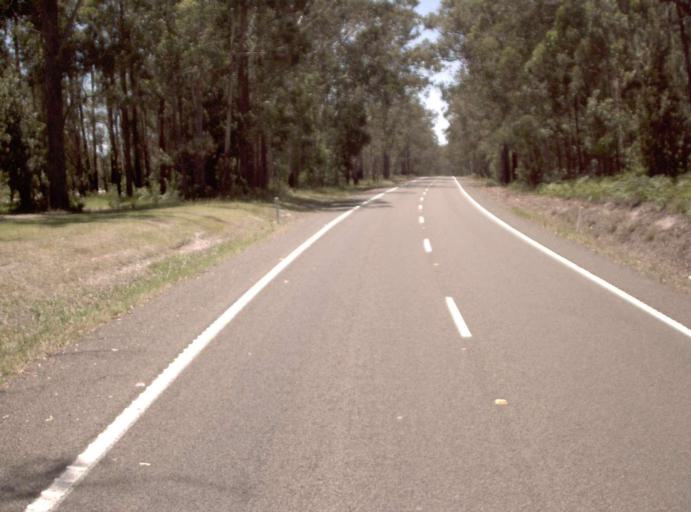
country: AU
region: Victoria
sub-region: East Gippsland
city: Lakes Entrance
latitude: -37.7741
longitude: 148.0523
